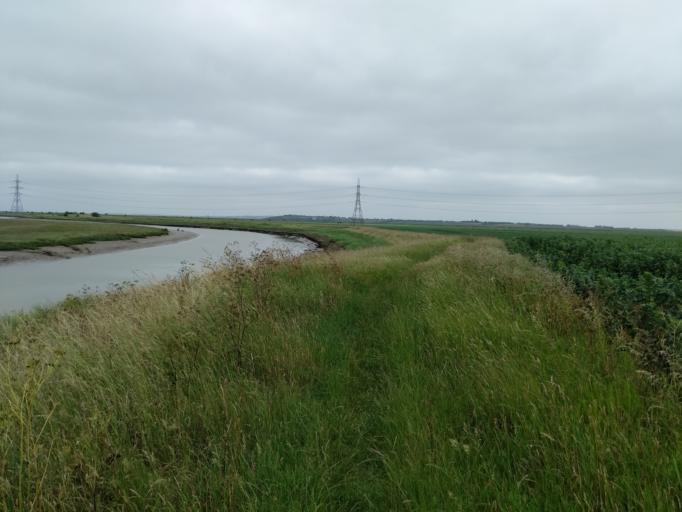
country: GB
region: England
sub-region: Kent
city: Faversham
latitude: 51.3333
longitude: 0.9126
